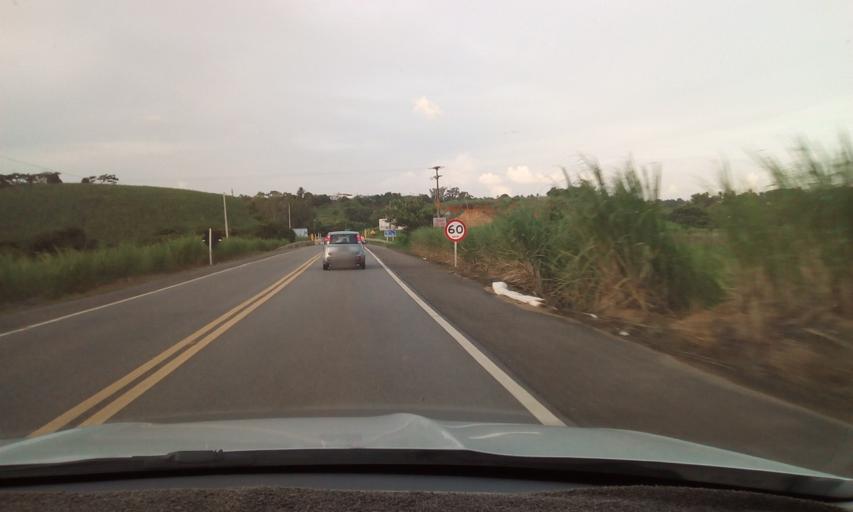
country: BR
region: Pernambuco
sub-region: Vicencia
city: Vicencia
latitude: -7.6186
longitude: -35.2409
